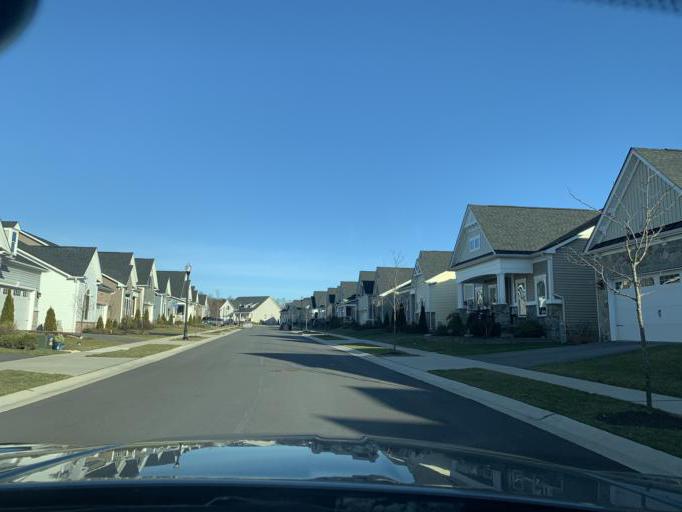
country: US
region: Maryland
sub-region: Anne Arundel County
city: Crofton
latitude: 39.0240
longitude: -76.7231
